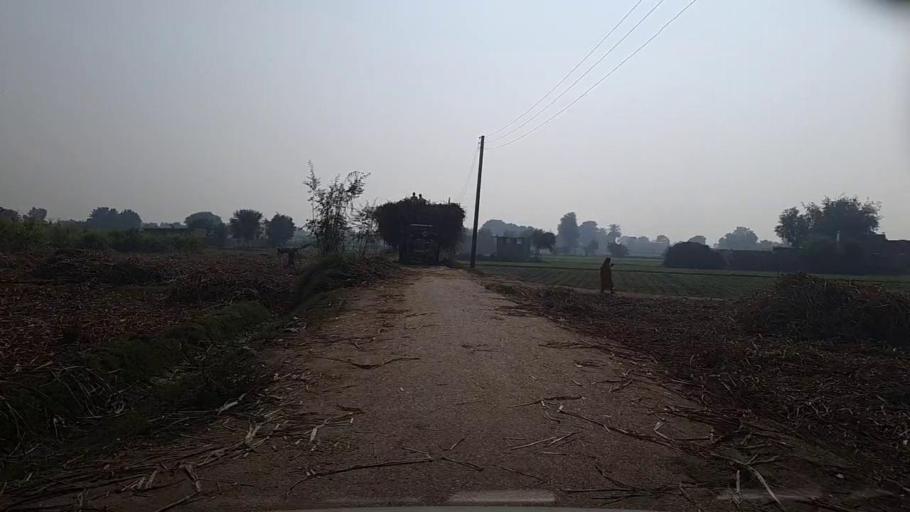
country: PK
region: Sindh
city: Setharja Old
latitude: 27.1298
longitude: 68.5146
